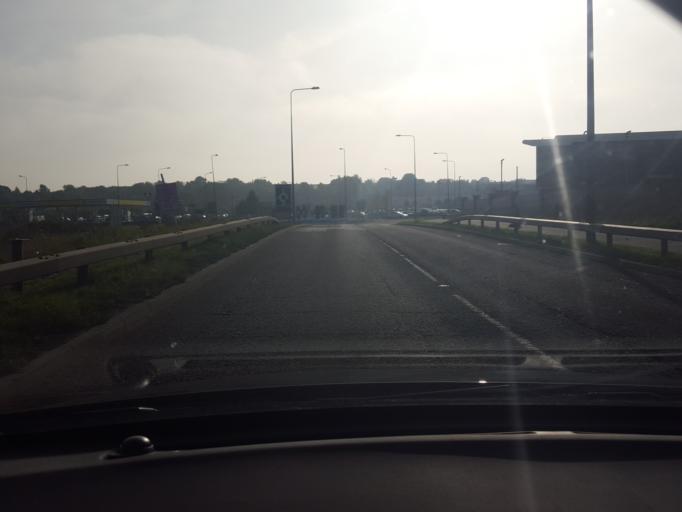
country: GB
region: England
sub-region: Suffolk
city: Shotley Gate
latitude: 51.9424
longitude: 1.2594
